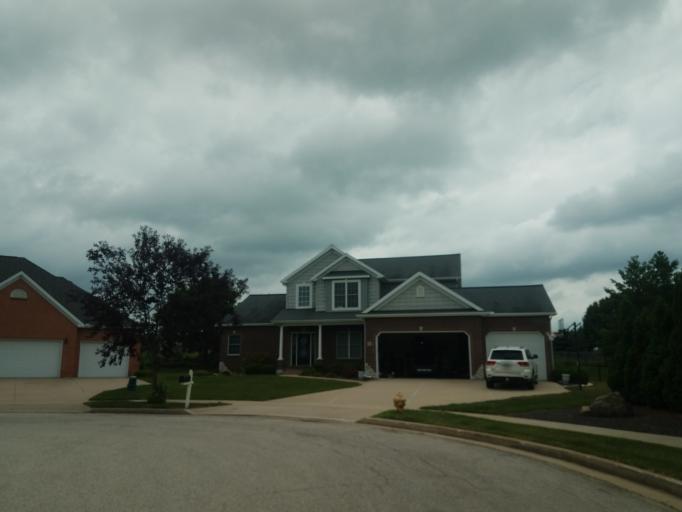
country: US
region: Illinois
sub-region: McLean County
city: Twin Grove
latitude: 40.4505
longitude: -89.0437
